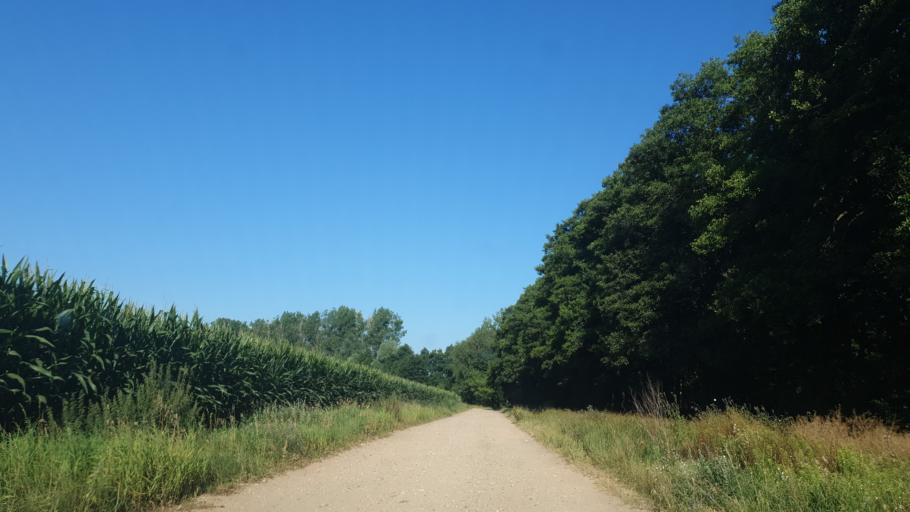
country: DE
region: Mecklenburg-Vorpommern
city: Ferdinandshof
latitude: 53.6533
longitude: 13.9512
